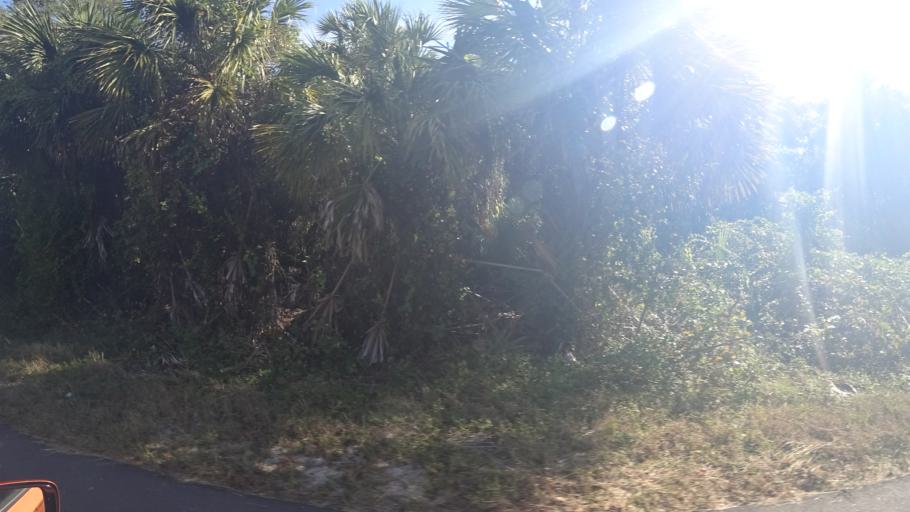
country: US
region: Florida
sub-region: Charlotte County
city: Port Charlotte
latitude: 27.0627
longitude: -82.1173
